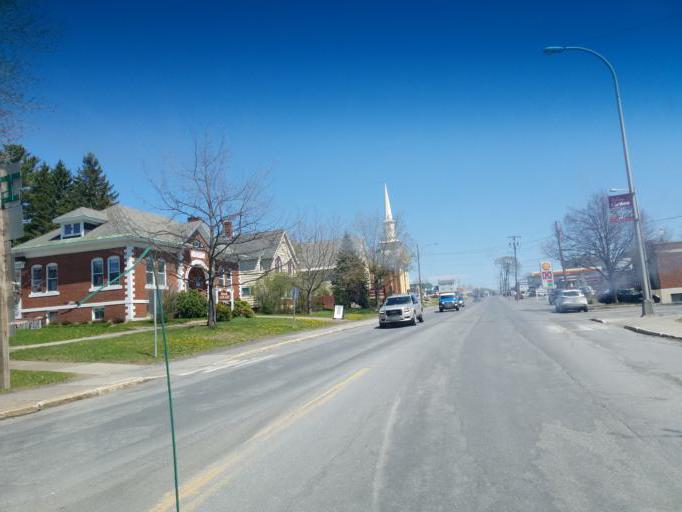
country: US
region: Maine
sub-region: Aroostook County
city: Caribou
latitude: 46.8606
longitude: -68.0116
